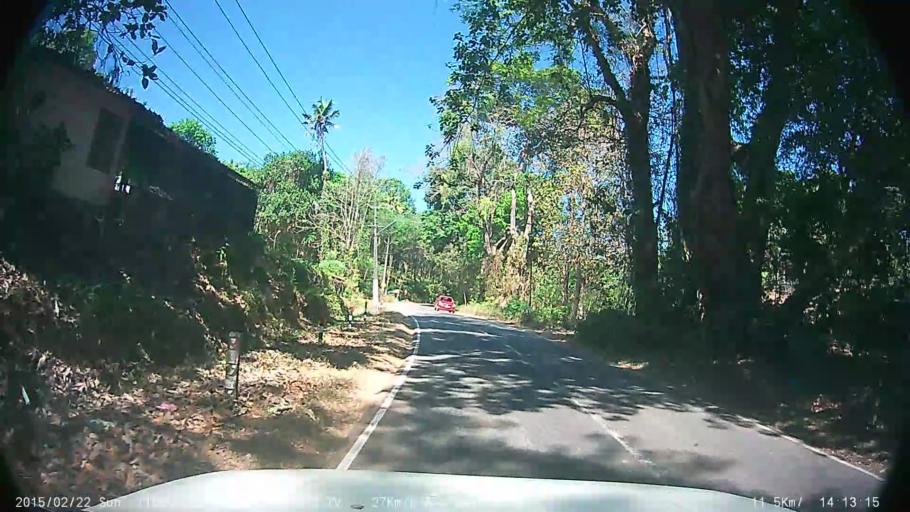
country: IN
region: Kerala
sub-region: Kottayam
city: Kottayam
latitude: 9.5381
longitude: 76.6795
